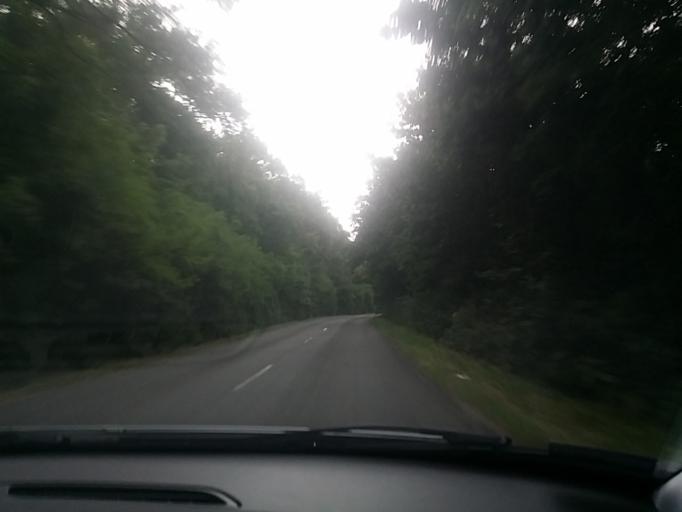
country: HU
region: Nograd
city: Paszto
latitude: 47.9199
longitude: 19.6312
